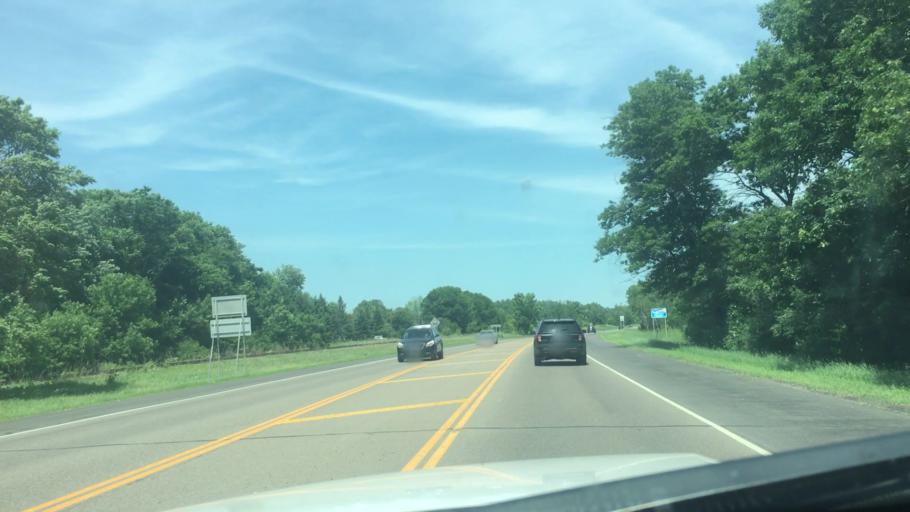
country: US
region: Minnesota
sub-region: Washington County
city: Hugo
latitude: 45.1253
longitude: -93.0030
